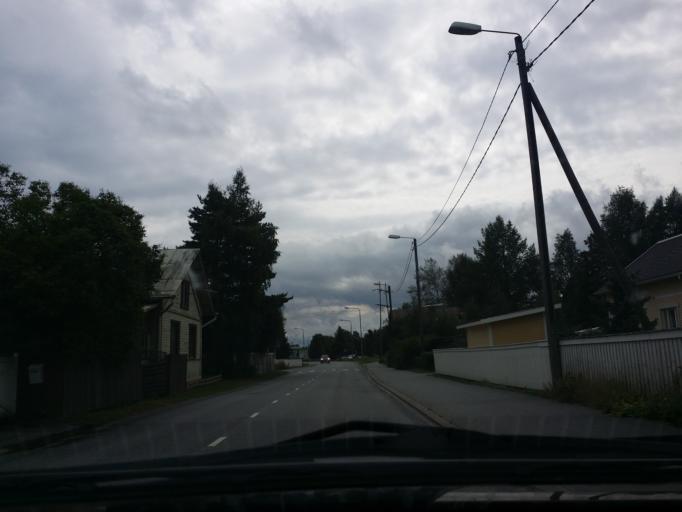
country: FI
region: Satakunta
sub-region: Pori
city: Pori
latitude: 61.5006
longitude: 21.8037
